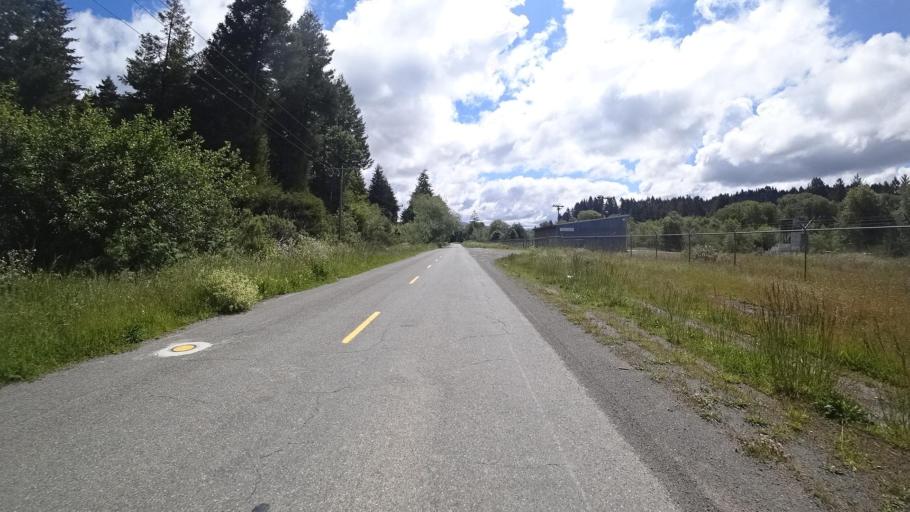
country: US
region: California
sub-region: Humboldt County
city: Arcata
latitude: 40.9068
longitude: -124.0430
